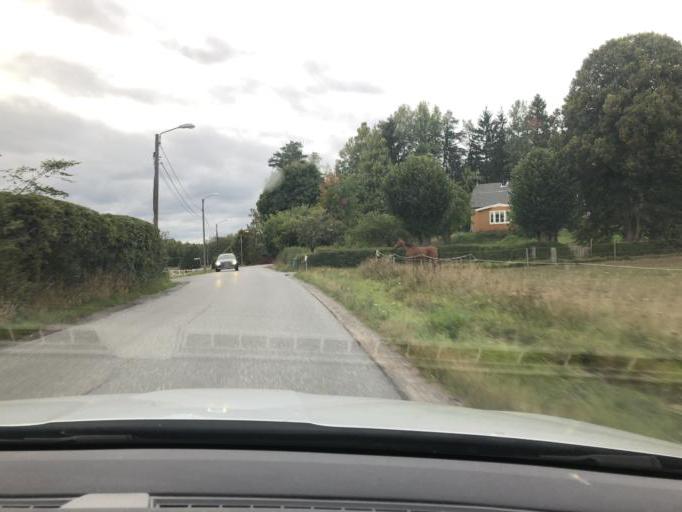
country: SE
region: Stockholm
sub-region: Haninge Kommun
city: Jordbro
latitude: 59.0954
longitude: 18.0369
